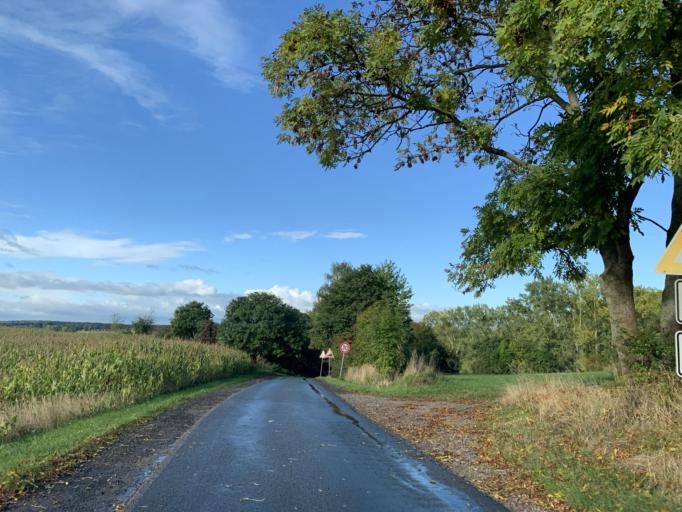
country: DE
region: Mecklenburg-Vorpommern
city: Burg Stargard
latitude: 53.4547
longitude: 13.2846
